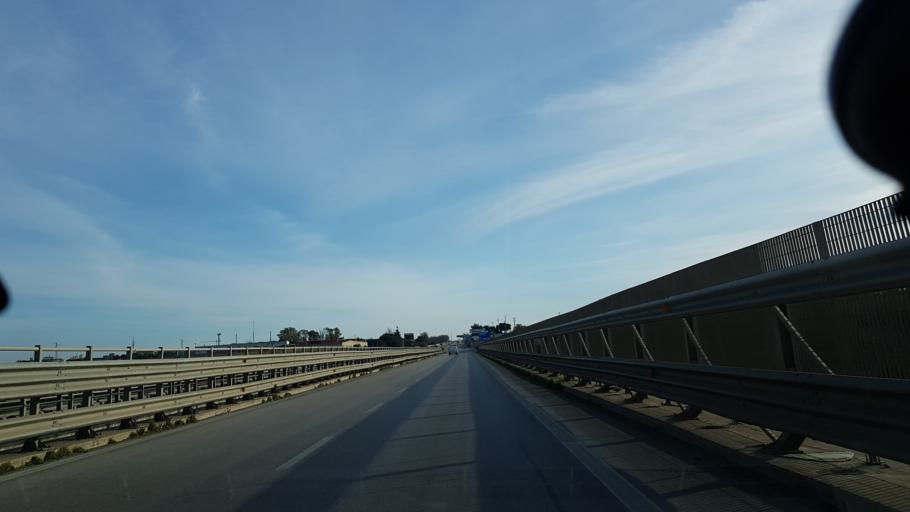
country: IT
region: Apulia
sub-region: Provincia di Brindisi
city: Brindisi
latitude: 40.6387
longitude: 17.9154
